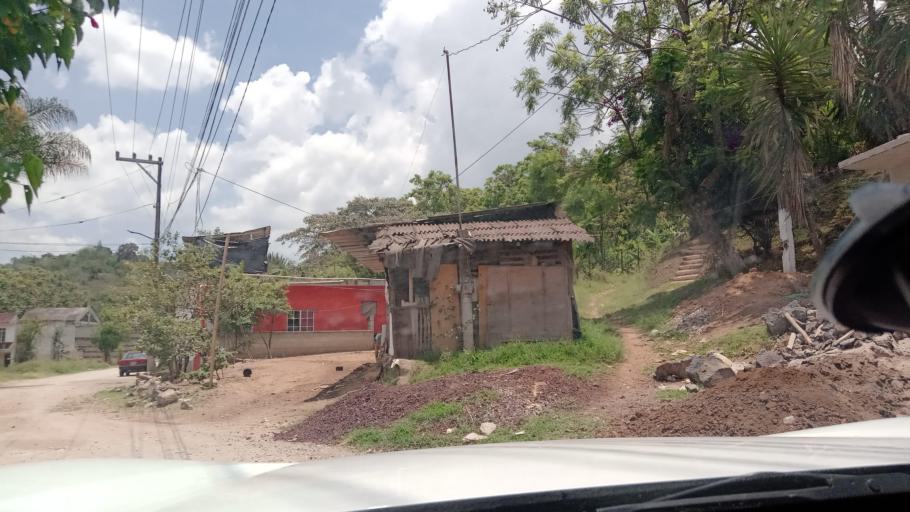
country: MX
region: Veracruz
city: Coatepec
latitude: 19.4311
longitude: -96.9780
